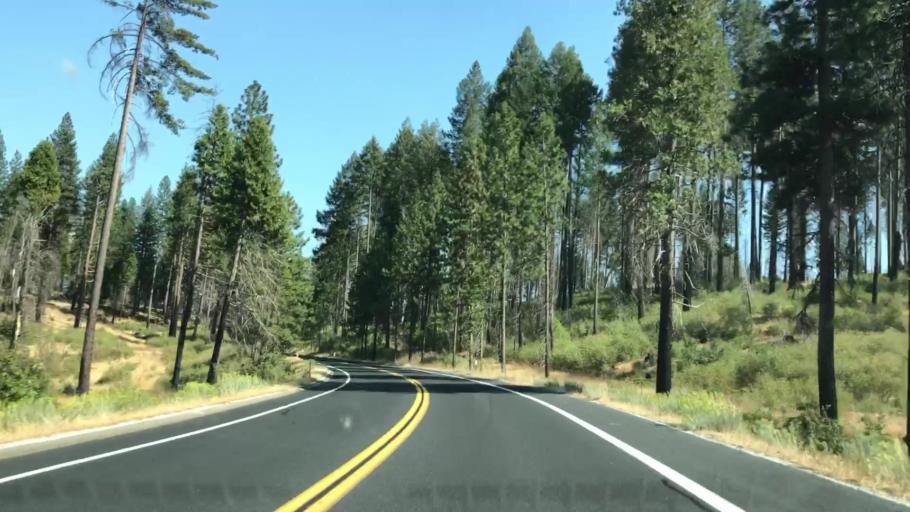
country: US
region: California
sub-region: Mariposa County
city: Midpines
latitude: 37.8253
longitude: -119.9723
